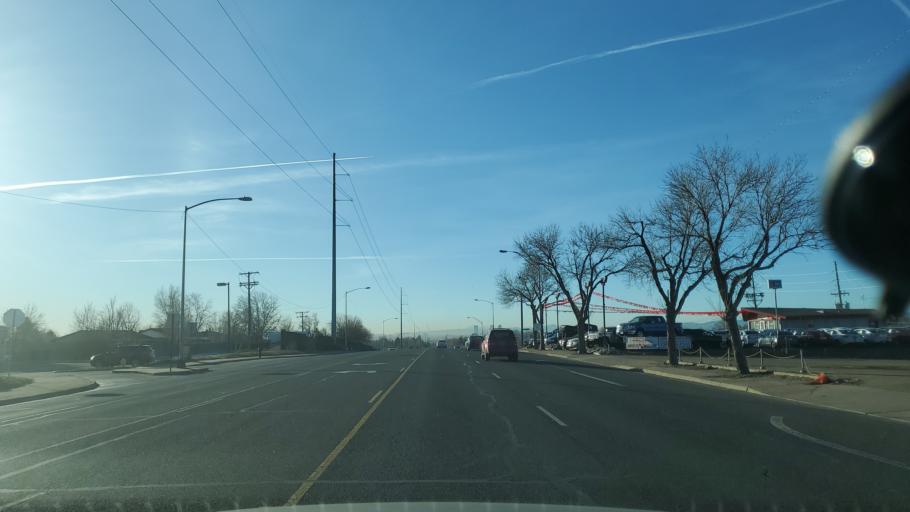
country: US
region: Colorado
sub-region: Adams County
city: Thornton
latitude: 39.8521
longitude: -104.9779
